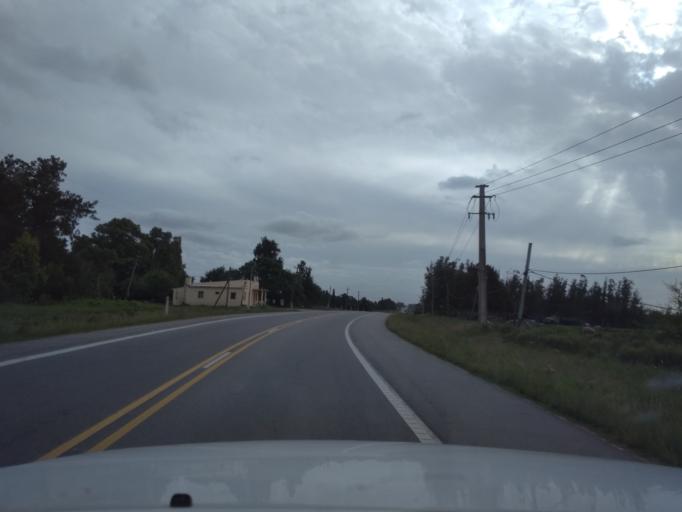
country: UY
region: Canelones
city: Joaquin Suarez
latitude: -34.7025
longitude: -56.0423
